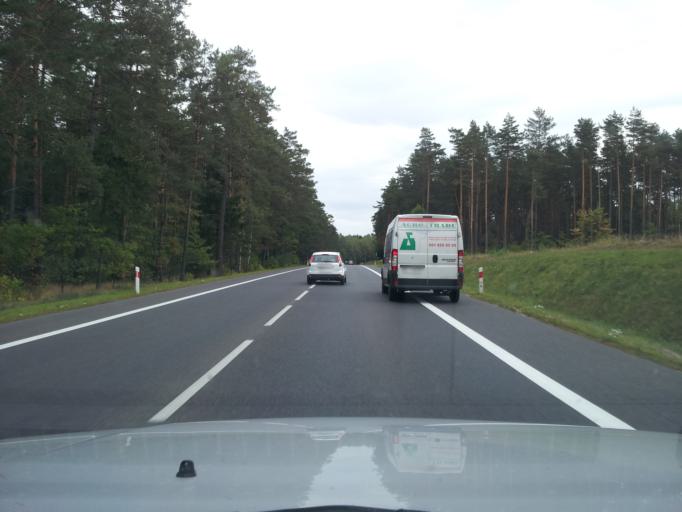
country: PL
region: Warmian-Masurian Voivodeship
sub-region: Powiat olsztynski
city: Gietrzwald
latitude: 53.7559
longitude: 20.2864
